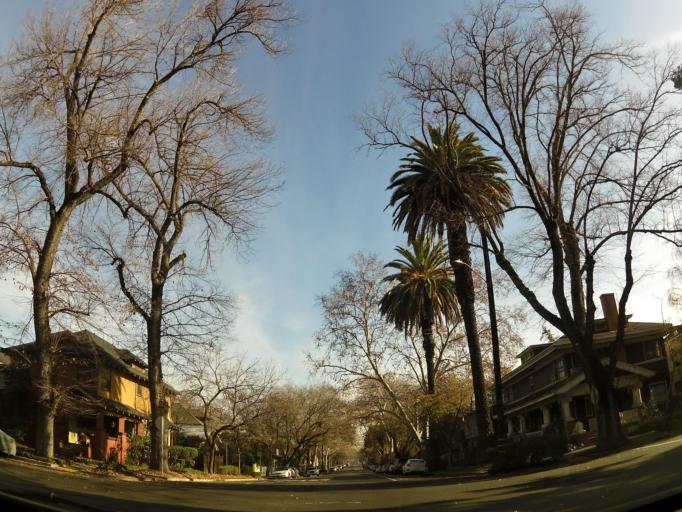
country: US
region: California
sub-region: Sacramento County
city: Sacramento
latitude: 38.5650
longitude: -121.4822
